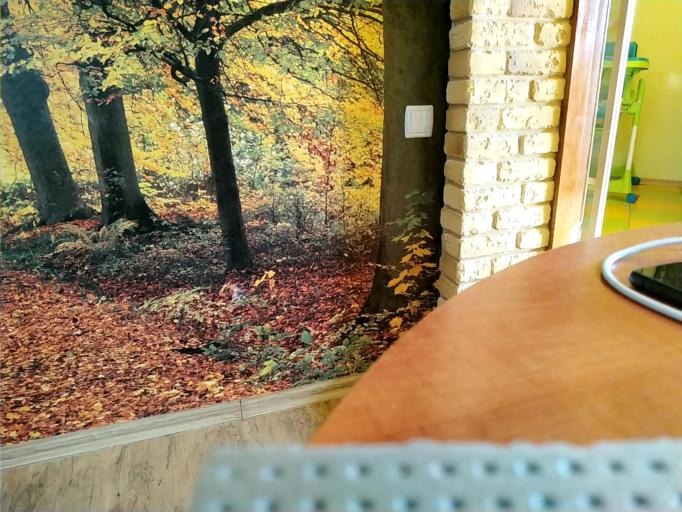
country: RU
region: Tverskaya
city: Kalashnikovo
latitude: 57.3482
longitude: 35.2028
